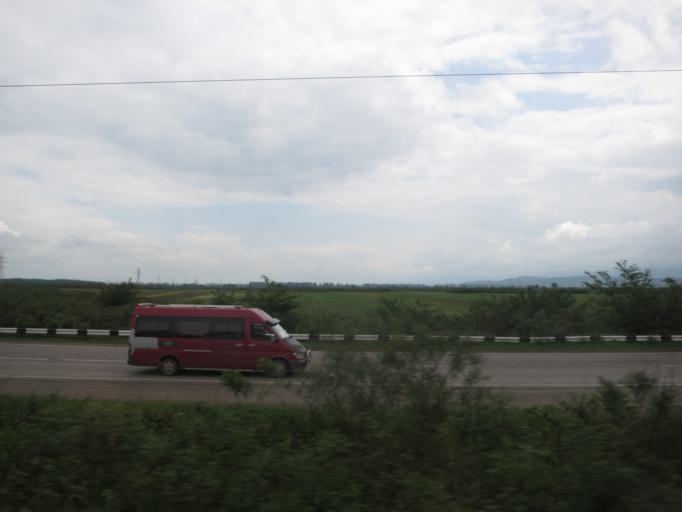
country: GE
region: Imereti
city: Samtredia
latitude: 42.1315
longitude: 42.3352
